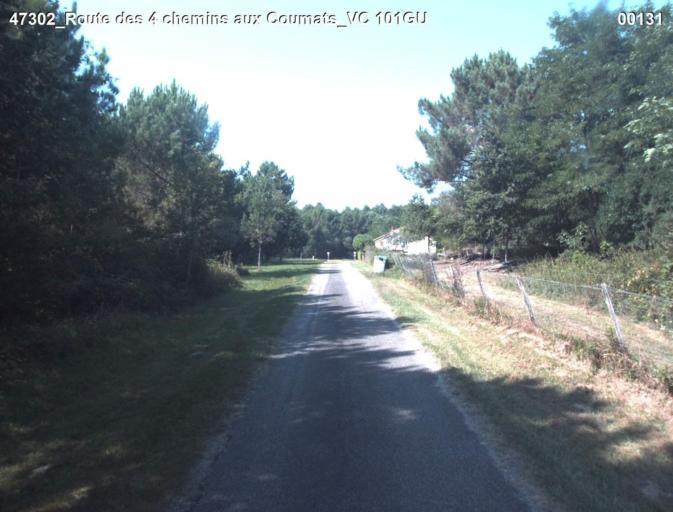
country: FR
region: Aquitaine
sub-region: Departement des Landes
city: Gabarret
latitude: 44.0209
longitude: 0.0851
